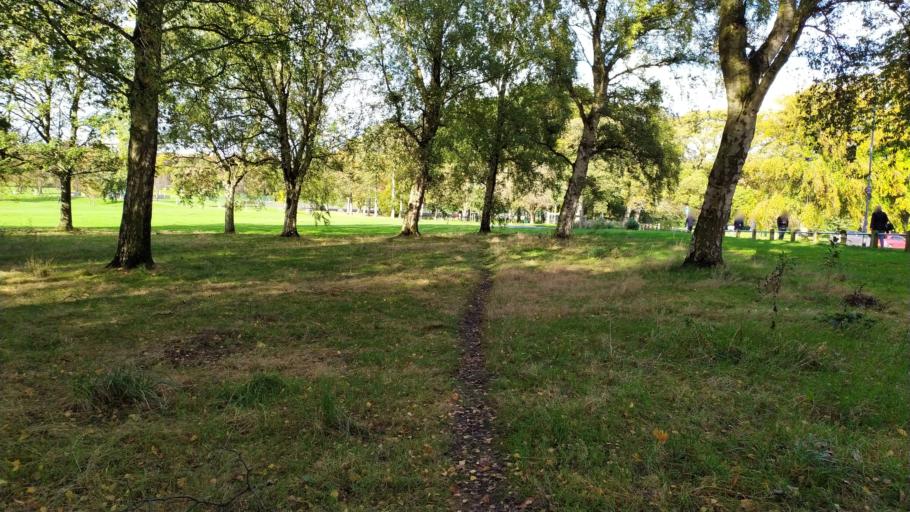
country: GB
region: England
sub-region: City and Borough of Leeds
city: Leeds
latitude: 53.8236
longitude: -1.5885
